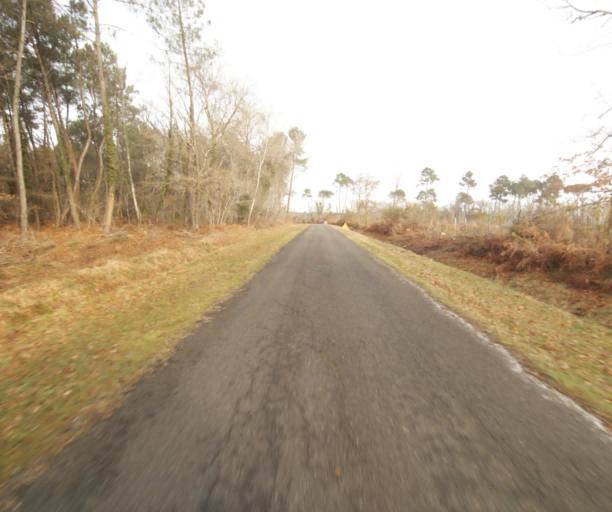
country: FR
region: Aquitaine
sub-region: Departement des Landes
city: Gabarret
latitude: 44.0846
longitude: 0.0716
